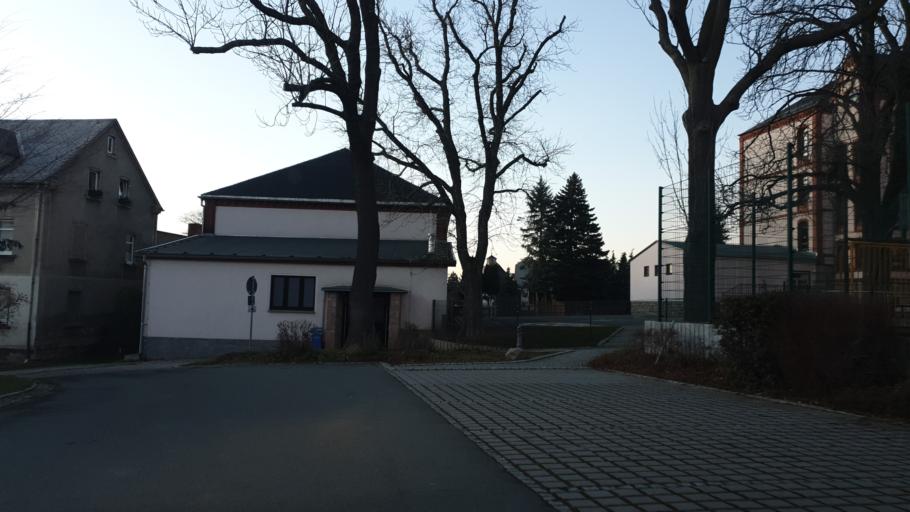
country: DE
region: Saxony
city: Hohndorf
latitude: 50.7449
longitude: 12.6730
